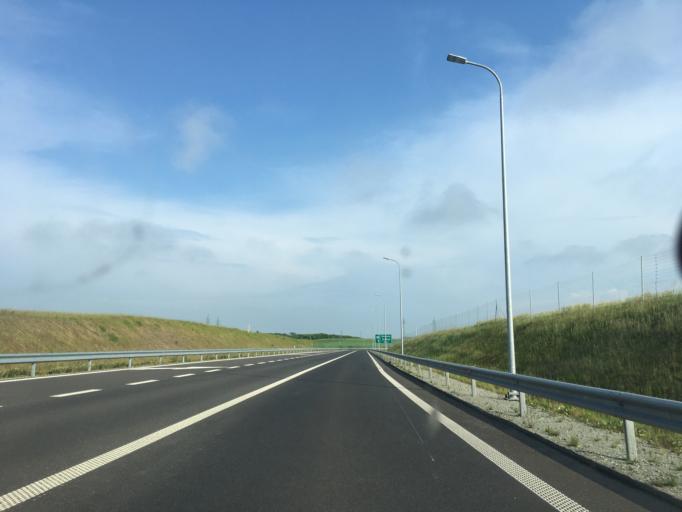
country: PL
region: West Pomeranian Voivodeship
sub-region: Koszalin
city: Koszalin
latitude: 54.1880
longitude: 16.1209
